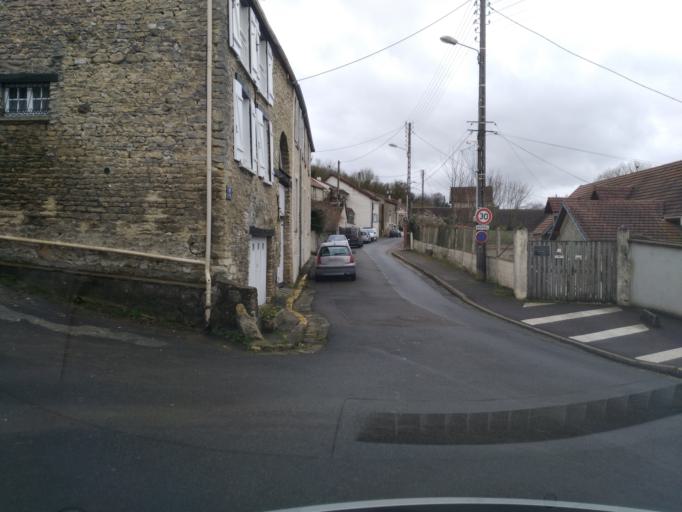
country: FR
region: Ile-de-France
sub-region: Departement des Yvelines
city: Mantes-la-Ville
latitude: 48.9532
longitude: 1.7103
